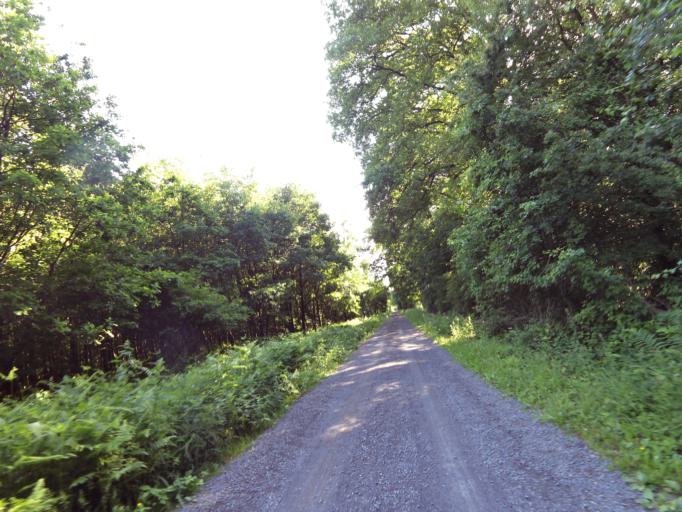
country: DE
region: North Rhine-Westphalia
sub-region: Regierungsbezirk Koln
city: Wachtberg
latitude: 50.6829
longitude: 7.1138
